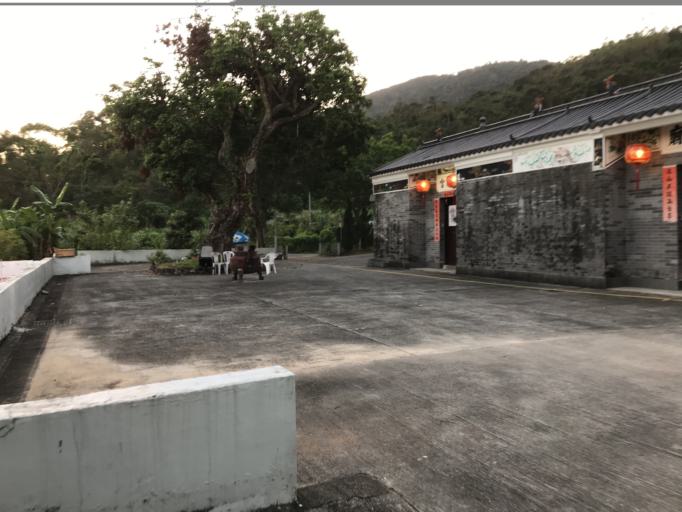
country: HK
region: Tai Po
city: Tai Po
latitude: 22.4696
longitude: 114.1469
